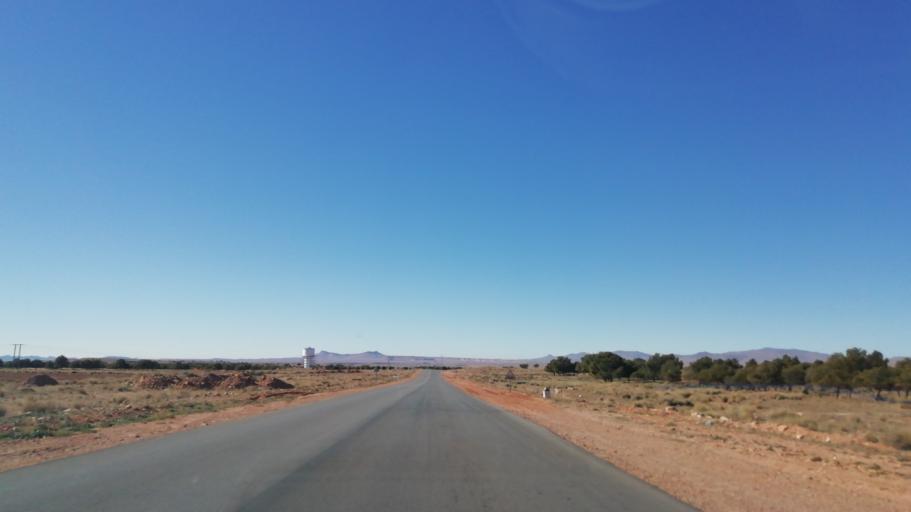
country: DZ
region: El Bayadh
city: El Bayadh
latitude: 33.6326
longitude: 1.3683
